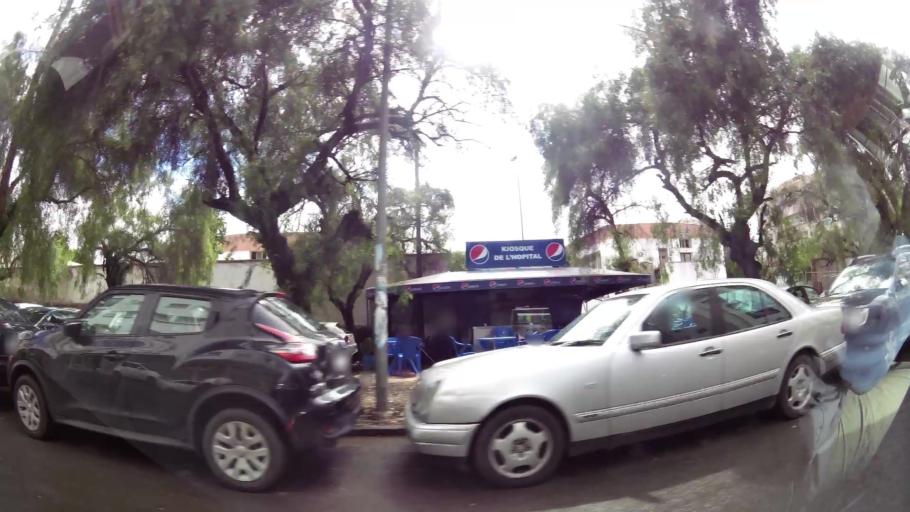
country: MA
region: Grand Casablanca
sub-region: Casablanca
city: Casablanca
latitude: 33.5788
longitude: -7.6230
